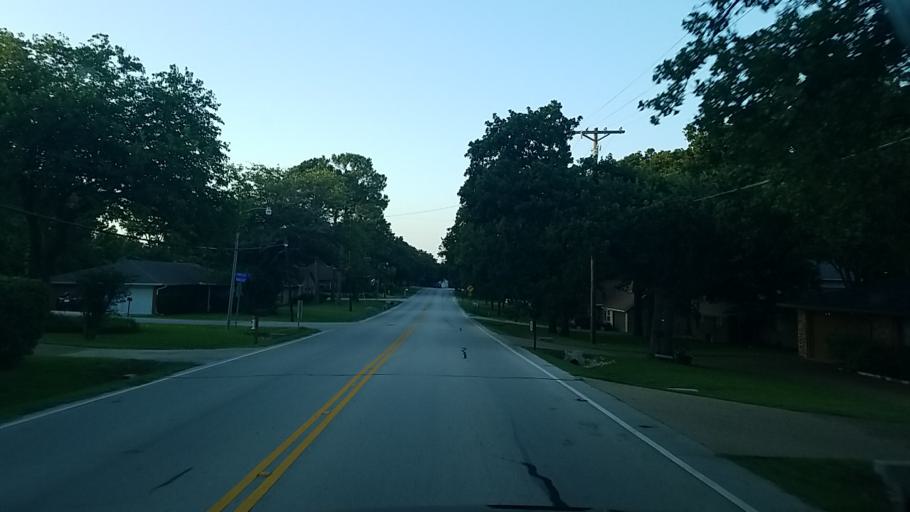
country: US
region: Texas
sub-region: Denton County
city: Highland Village
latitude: 33.0914
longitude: -97.0508
